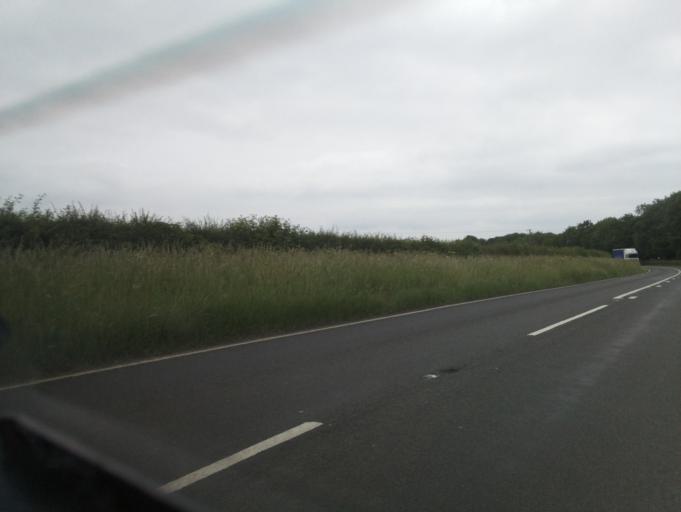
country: GB
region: England
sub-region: District of Rutland
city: Empingham
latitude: 52.6658
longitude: -0.6186
